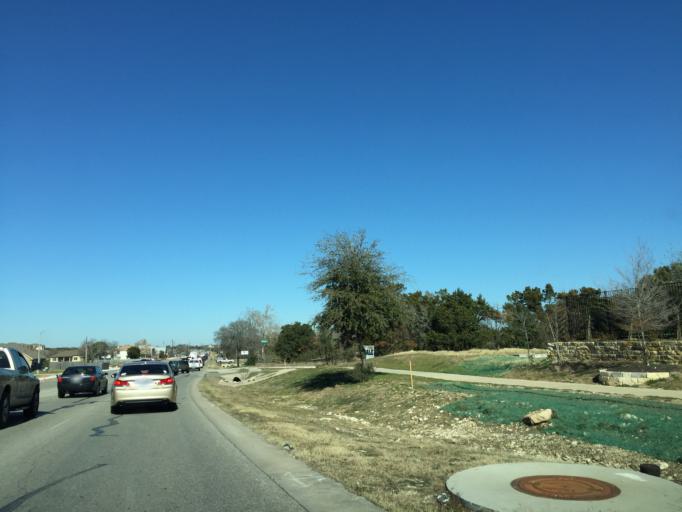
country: US
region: Texas
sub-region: Williamson County
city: Leander
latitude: 30.5532
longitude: -97.8572
